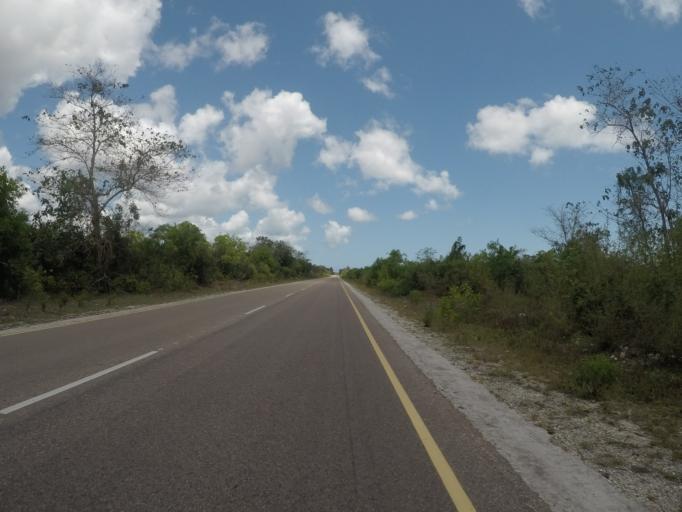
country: TZ
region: Zanzibar Central/South
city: Koani
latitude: -6.2612
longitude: 39.3592
